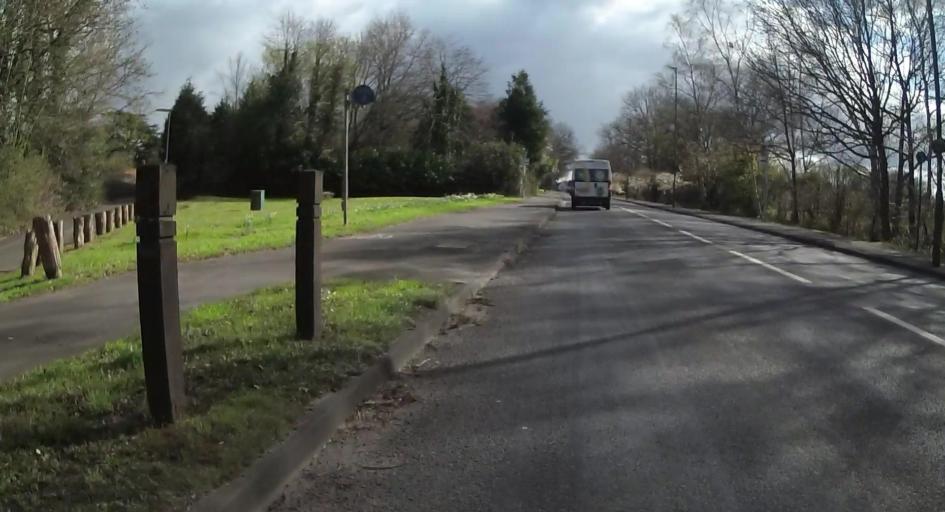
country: GB
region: England
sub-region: Surrey
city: Knaphill
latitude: 51.3305
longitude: -0.6388
